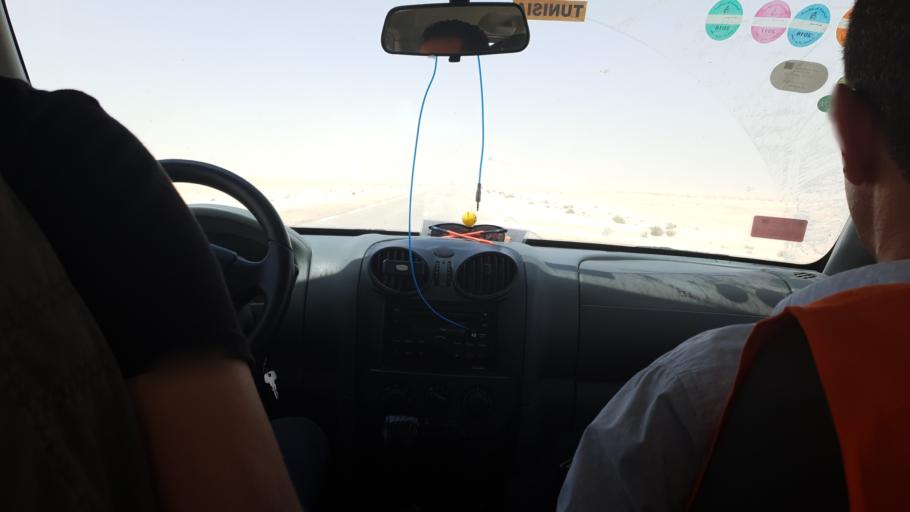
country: TN
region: Qibili
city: Kebili
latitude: 33.8712
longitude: 8.6016
